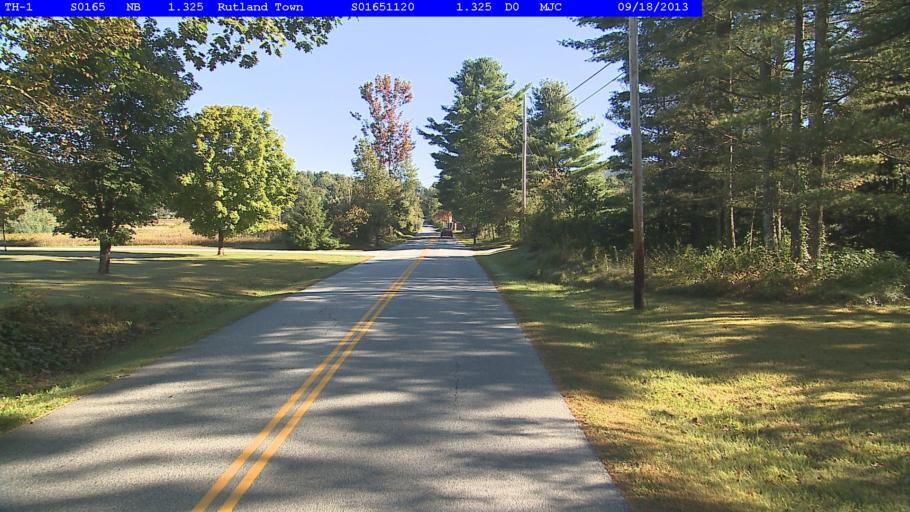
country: US
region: Vermont
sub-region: Rutland County
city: Rutland
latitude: 43.6589
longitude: -72.9515
